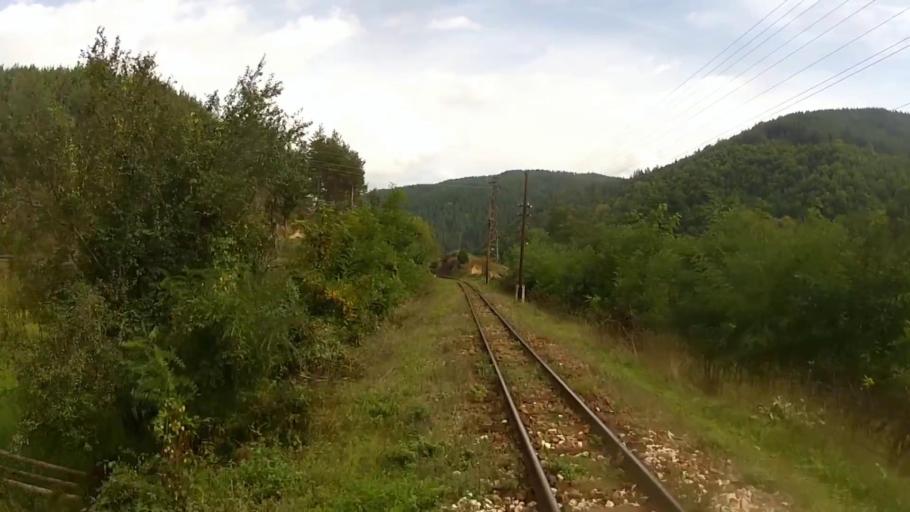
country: BG
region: Blagoevgrad
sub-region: Obshtina Yakoruda
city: Yakoruda
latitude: 42.0378
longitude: 23.7088
